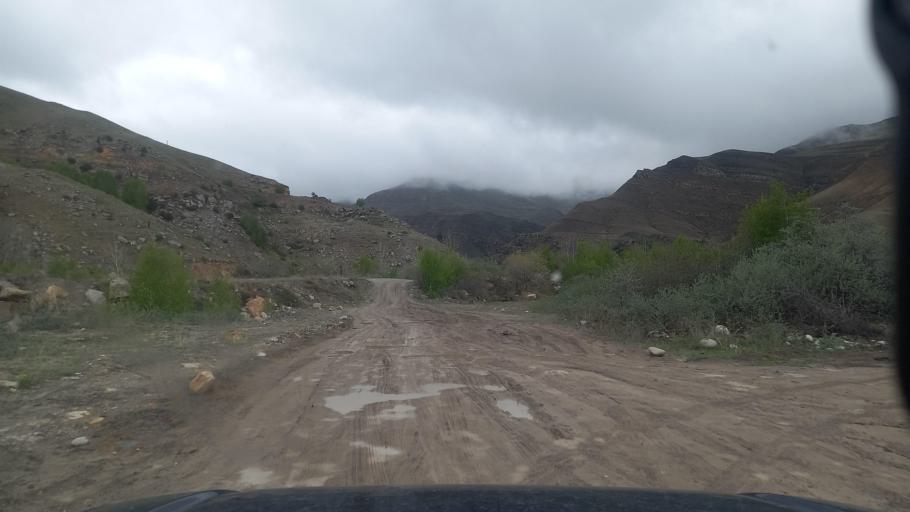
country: RU
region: Kabardino-Balkariya
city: Bylym
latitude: 43.4593
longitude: 42.9948
